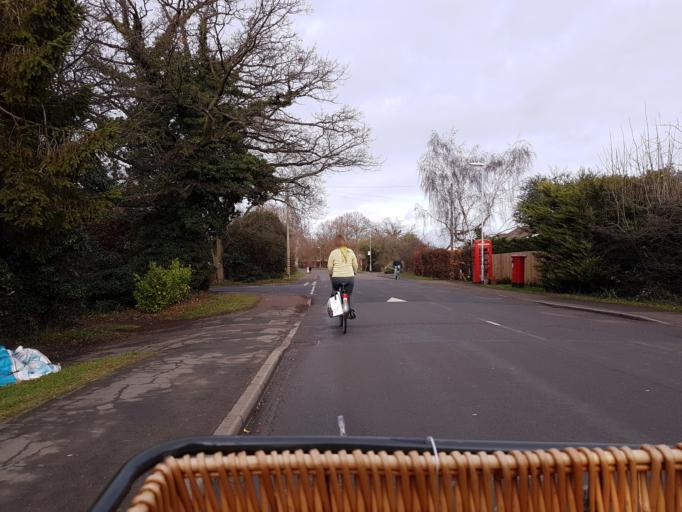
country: GB
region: England
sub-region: Cambridgeshire
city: Girton
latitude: 52.2339
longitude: 0.0861
